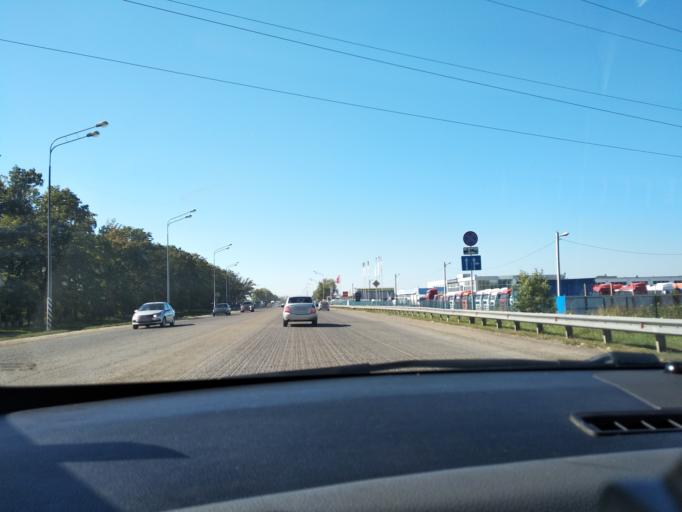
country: RU
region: Krasnodarskiy
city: Krasnodar
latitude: 45.1359
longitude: 39.0293
